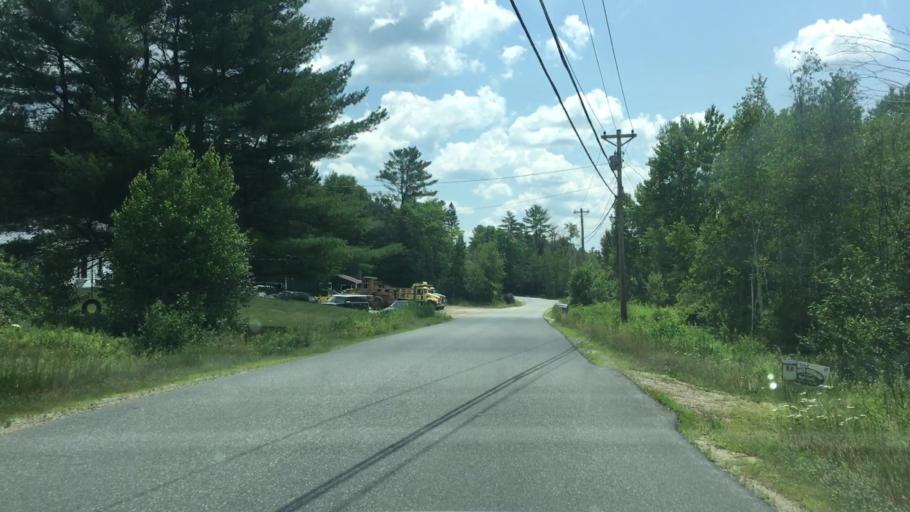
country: US
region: New Hampshire
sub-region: Grafton County
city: Enfield
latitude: 43.6612
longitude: -72.0995
